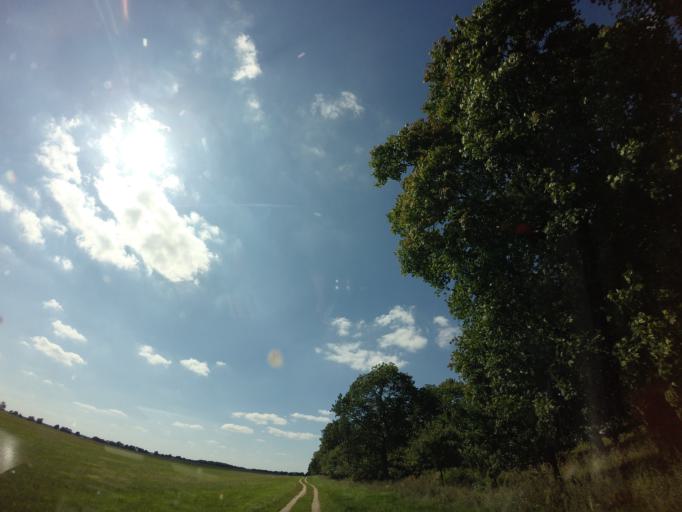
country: PL
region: West Pomeranian Voivodeship
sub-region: Powiat choszczenski
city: Recz
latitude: 53.2679
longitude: 15.6377
